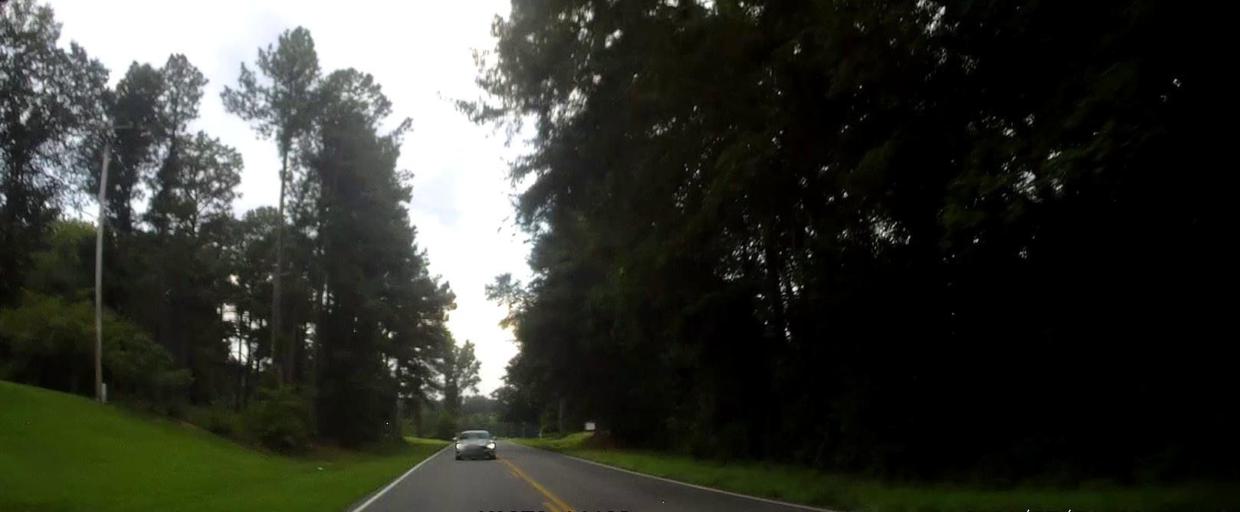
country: US
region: Georgia
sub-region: Laurens County
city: Dublin
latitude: 32.5896
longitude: -82.9002
